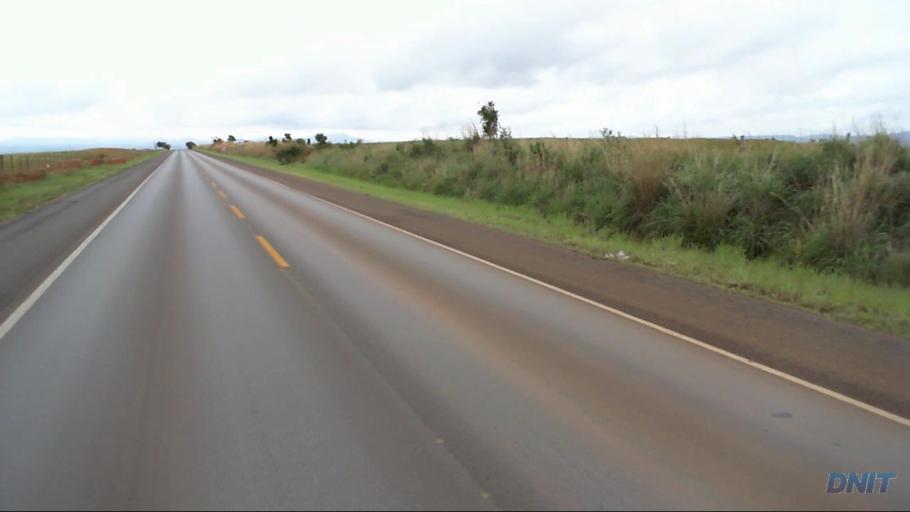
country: BR
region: Goias
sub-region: Padre Bernardo
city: Padre Bernardo
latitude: -15.2118
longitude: -48.4903
